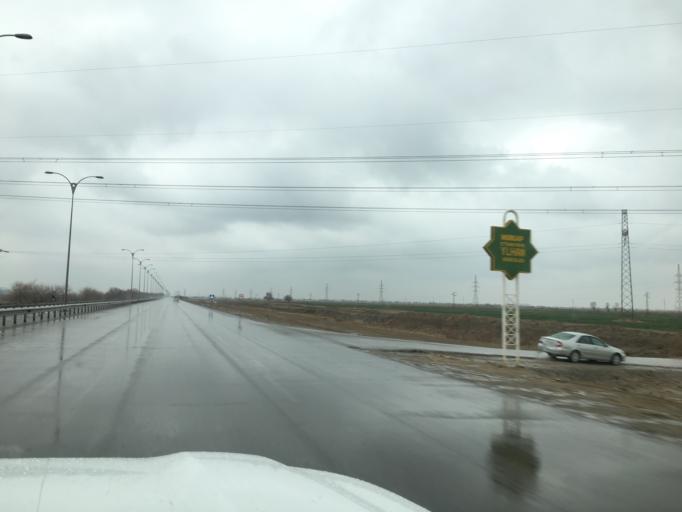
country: TM
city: Murgab
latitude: 37.5235
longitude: 61.9109
